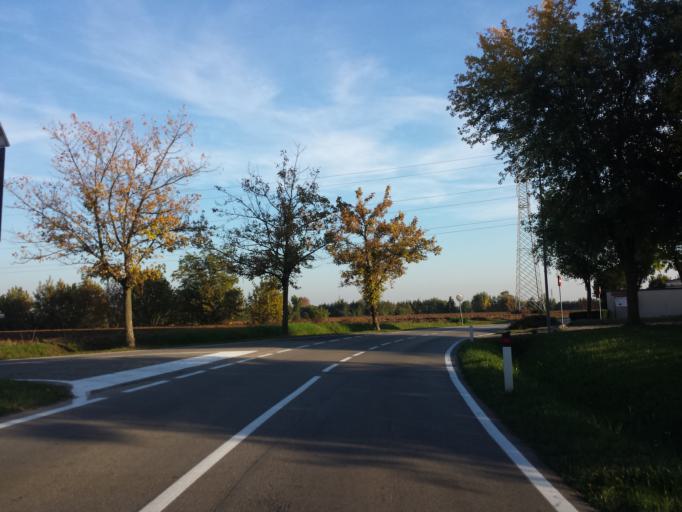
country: IT
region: Veneto
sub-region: Provincia di Vicenza
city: Motta
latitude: 45.5942
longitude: 11.5052
